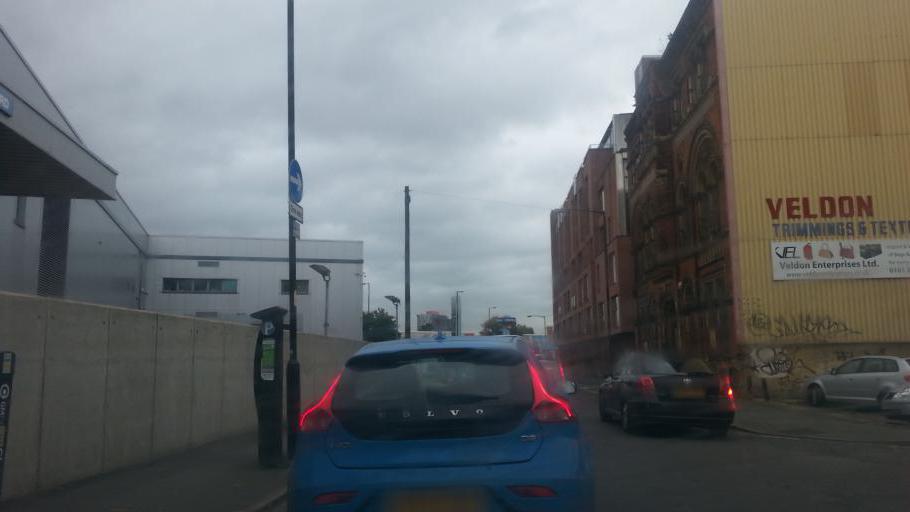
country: GB
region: England
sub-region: Manchester
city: Manchester
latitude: 53.4810
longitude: -2.2284
